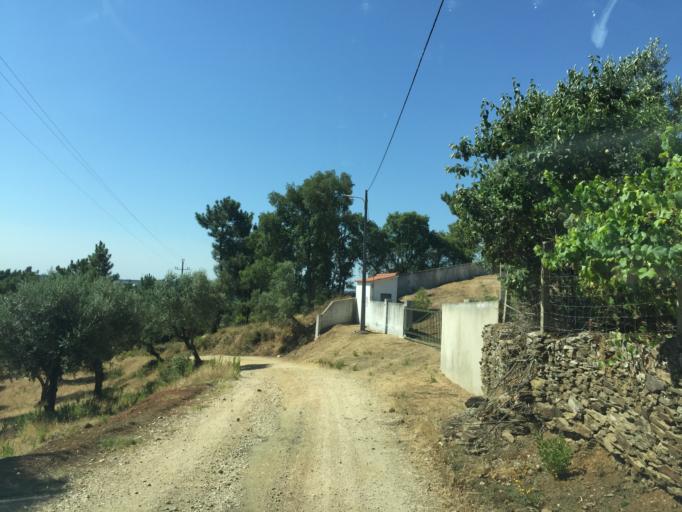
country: PT
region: Santarem
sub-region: Ferreira do Zezere
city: Ferreira do Zezere
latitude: 39.5848
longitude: -8.2768
